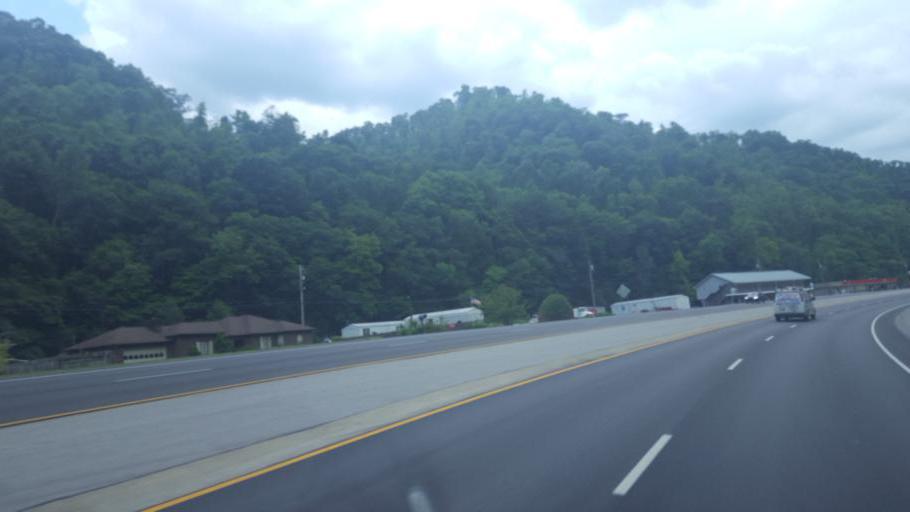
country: US
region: Kentucky
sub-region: Pike County
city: Pikeville
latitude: 37.3434
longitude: -82.5485
